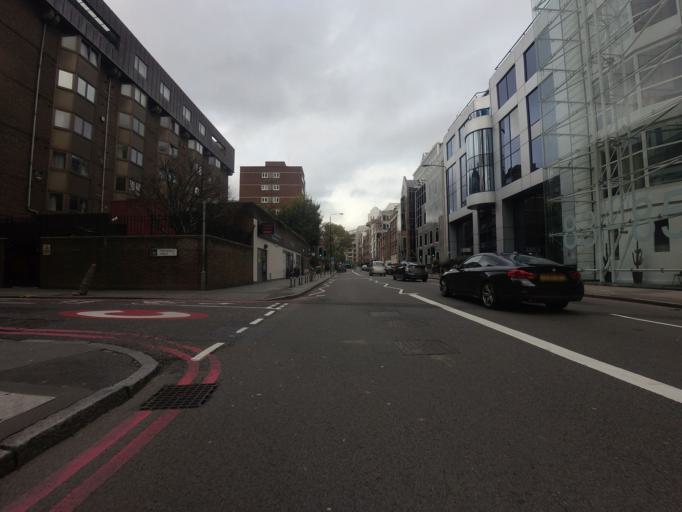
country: GB
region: England
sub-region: Greater London
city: City of London
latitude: 51.5117
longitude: -0.0731
